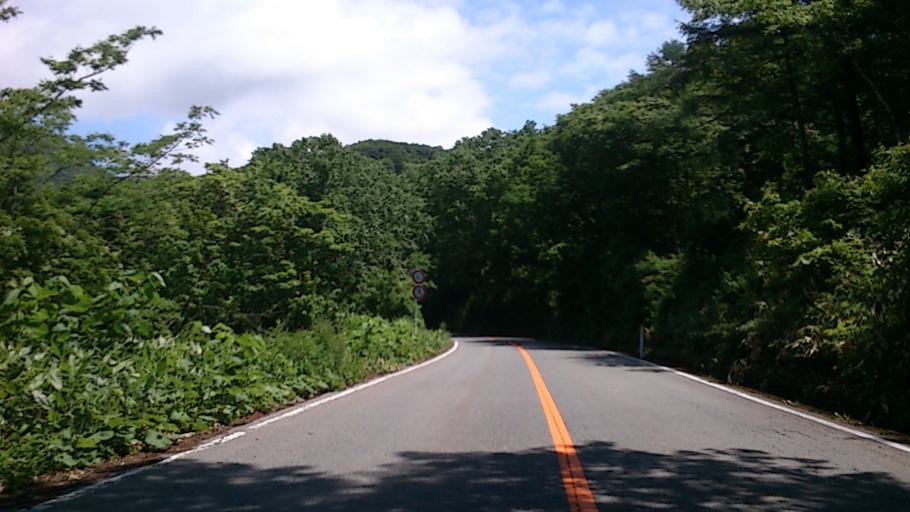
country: JP
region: Yamagata
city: Yamagata-shi
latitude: 38.1211
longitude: 140.4062
